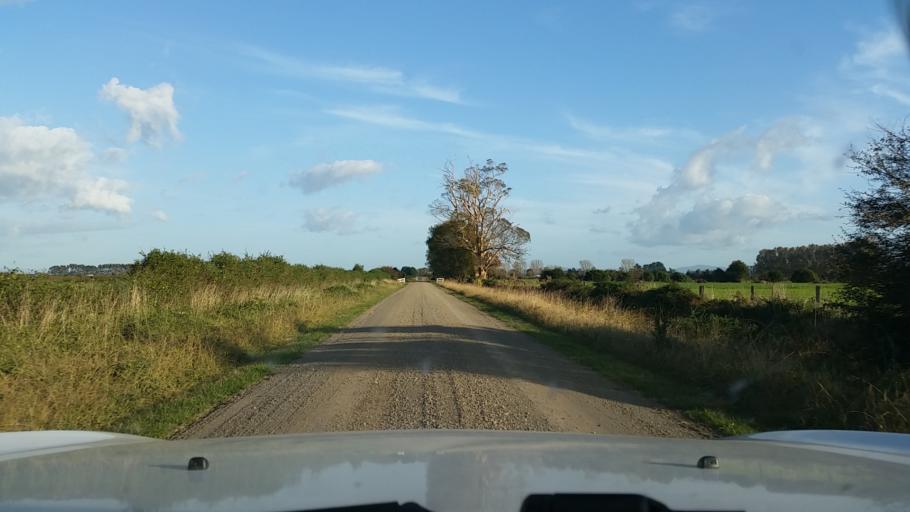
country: NZ
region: Bay of Plenty
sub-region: Western Bay of Plenty District
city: Katikati
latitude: -37.5867
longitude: 175.7131
